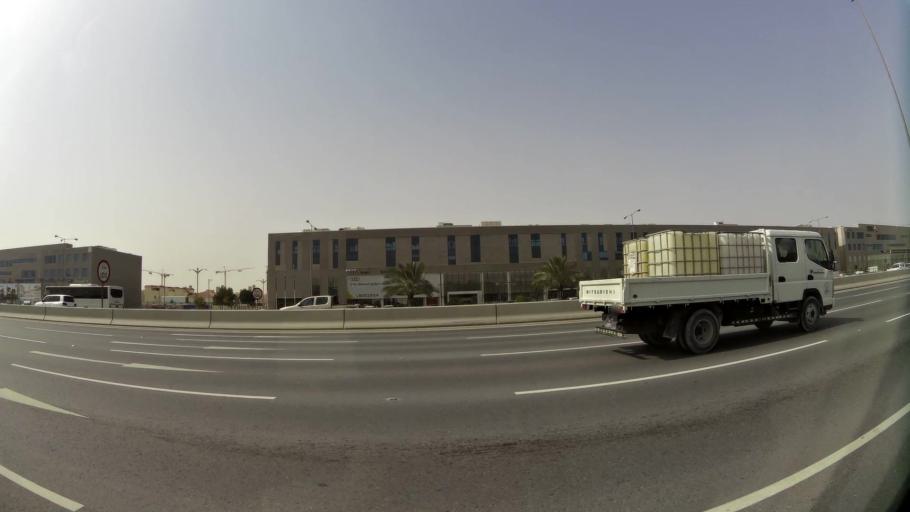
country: QA
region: Baladiyat ad Dawhah
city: Doha
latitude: 25.2534
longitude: 51.4797
